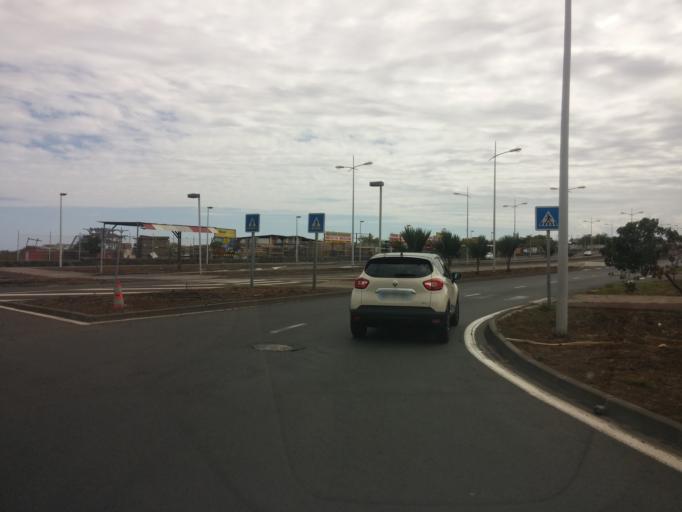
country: RE
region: Reunion
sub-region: Reunion
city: Le Port
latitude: -20.9709
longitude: 55.2962
